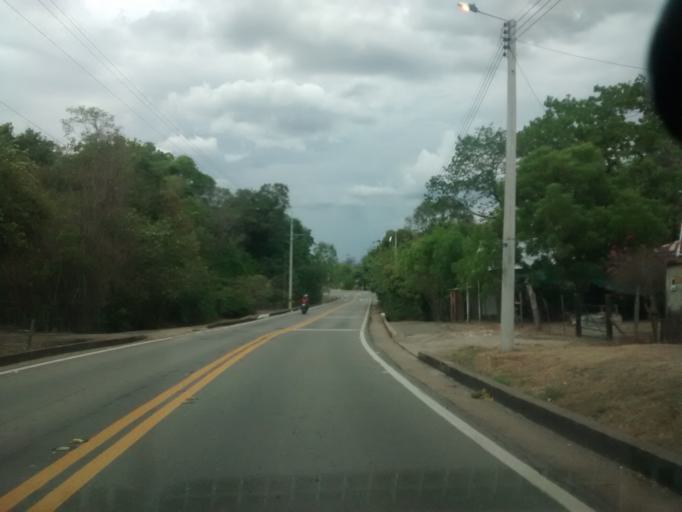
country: CO
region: Cundinamarca
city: Agua de Dios
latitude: 4.4259
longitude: -74.6993
